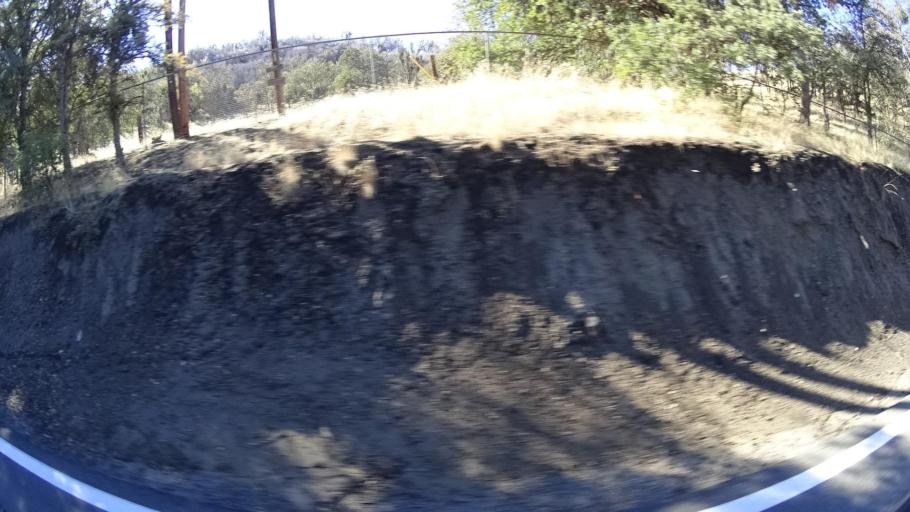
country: US
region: California
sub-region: Kern County
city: Alta Sierra
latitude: 35.7216
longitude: -118.6944
